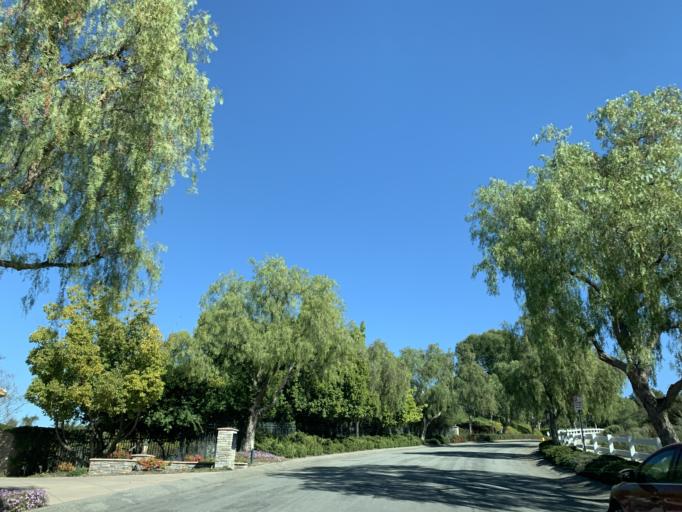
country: US
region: California
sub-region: Orange County
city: Brea
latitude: 33.8927
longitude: -117.9059
